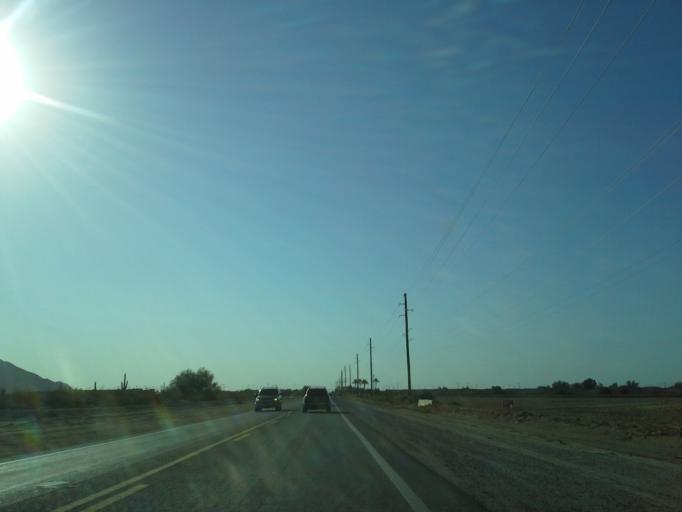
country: US
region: Arizona
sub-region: Pinal County
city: San Tan Valley
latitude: 33.1733
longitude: -111.5759
